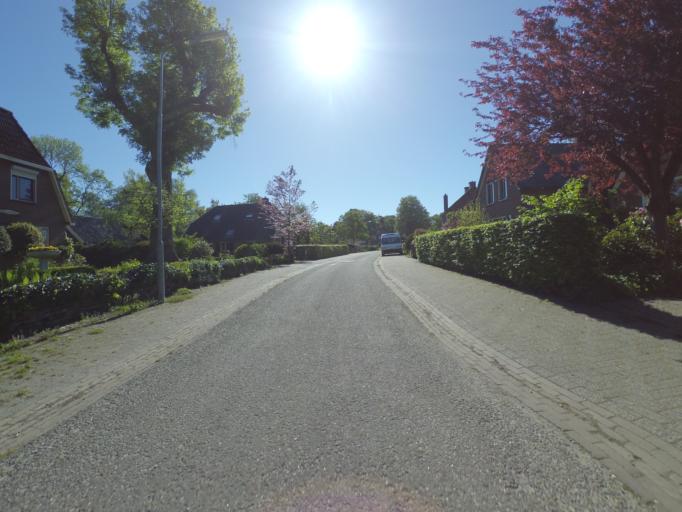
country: NL
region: Gelderland
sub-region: Gemeente Brummen
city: Eerbeek
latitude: 52.1137
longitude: 6.0996
